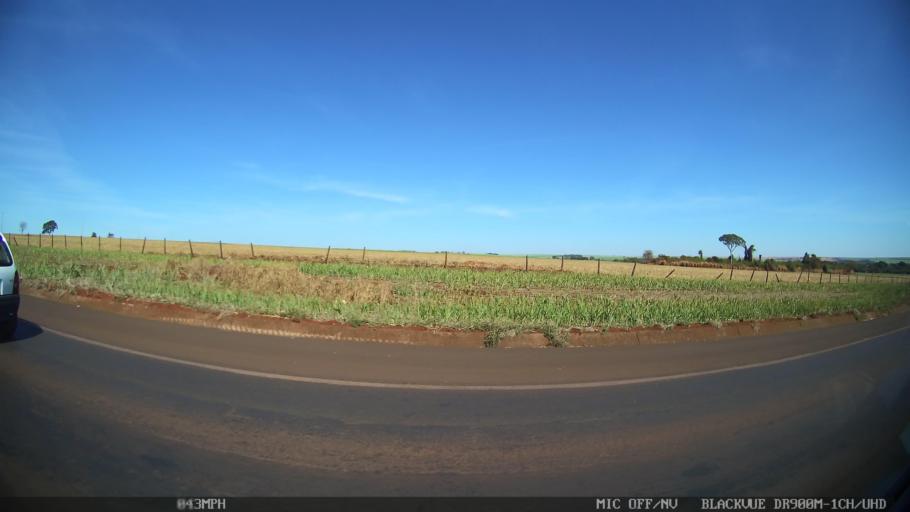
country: BR
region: Sao Paulo
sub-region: Sao Joaquim Da Barra
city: Sao Joaquim da Barra
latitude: -20.5074
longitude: -47.9226
